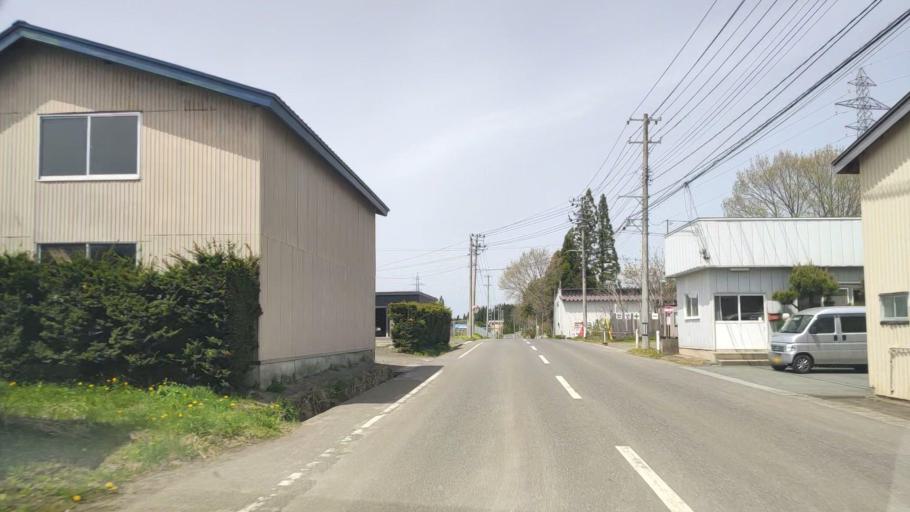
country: JP
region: Aomori
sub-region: Misawa Shi
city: Inuotose
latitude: 40.7199
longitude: 141.1423
